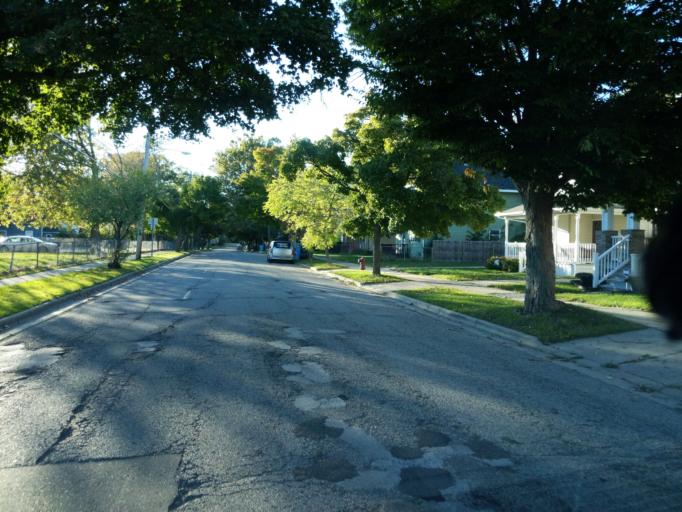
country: US
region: Michigan
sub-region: Ingham County
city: Lansing
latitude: 42.7327
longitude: -84.5699
